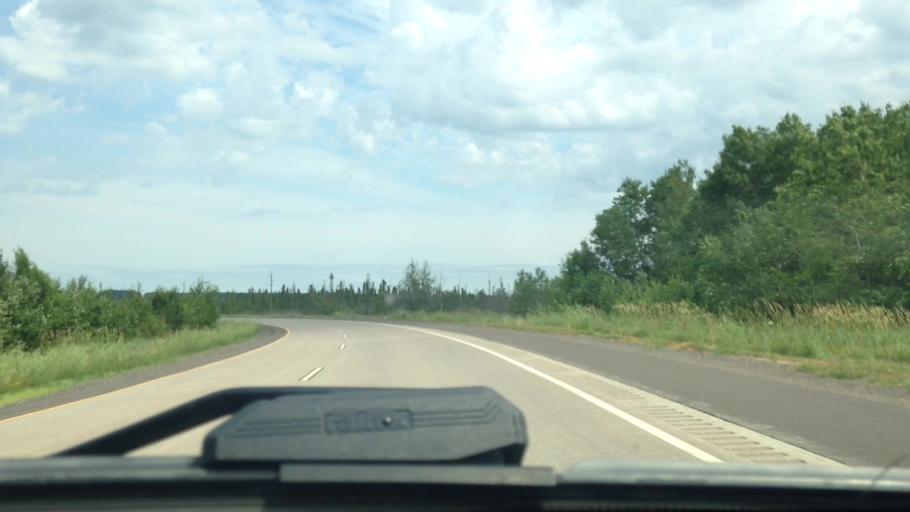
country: US
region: Wisconsin
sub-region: Douglas County
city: Lake Nebagamon
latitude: 46.2596
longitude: -91.8002
